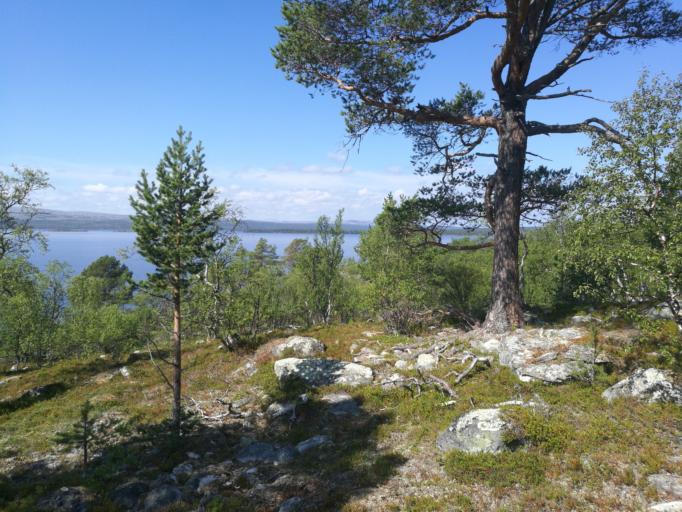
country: NO
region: Sor-Trondelag
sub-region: Roros
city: Roros
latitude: 62.3968
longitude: 11.9780
